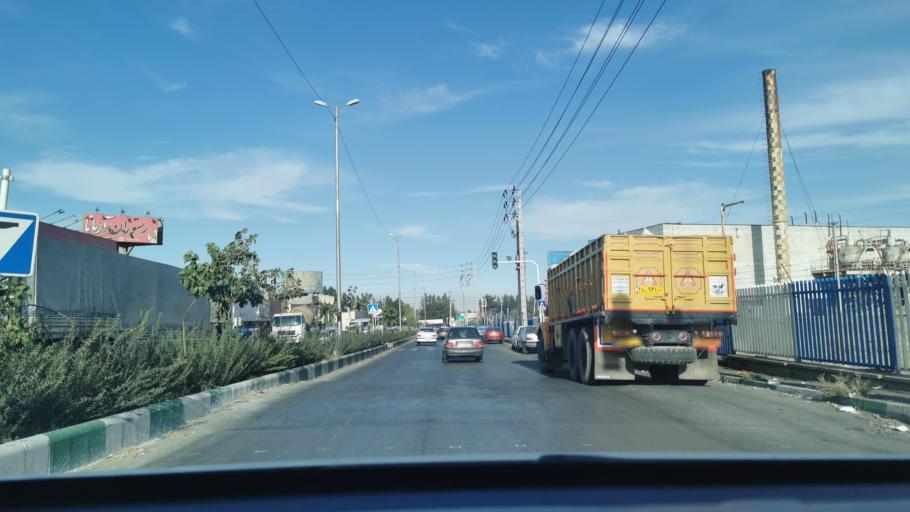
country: IR
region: Razavi Khorasan
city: Torqabeh
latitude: 36.4380
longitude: 59.4401
